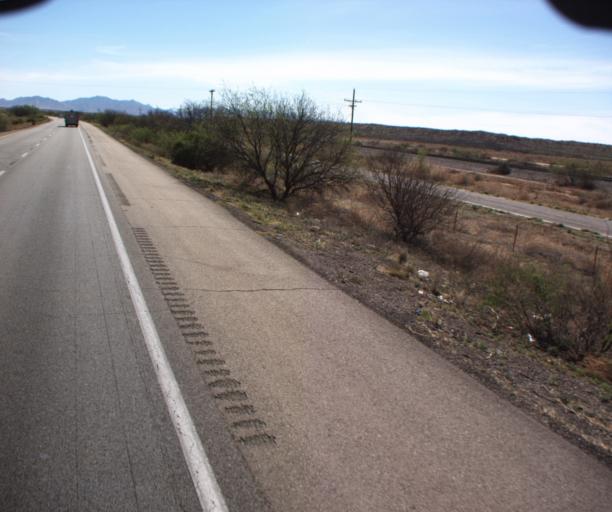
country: US
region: Arizona
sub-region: Cochise County
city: Benson
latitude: 31.9651
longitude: -110.2623
